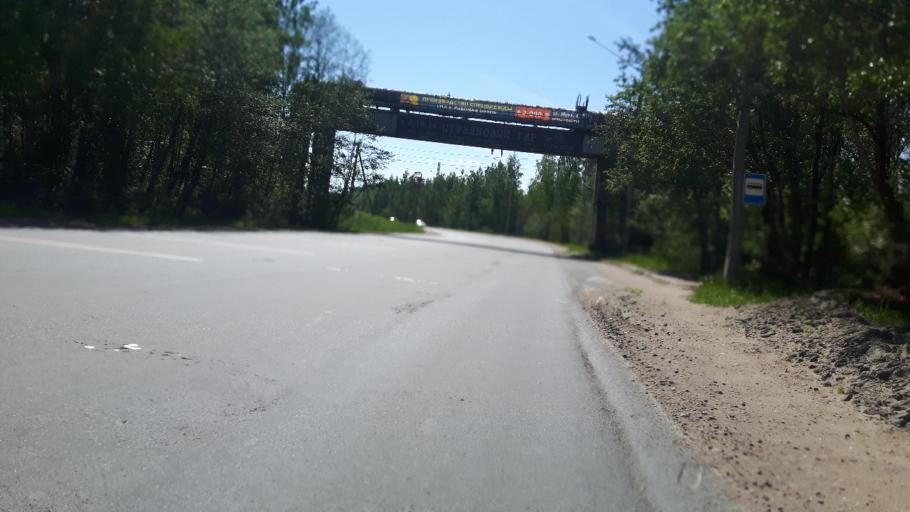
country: RU
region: Leningrad
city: Sosnovyy Bor
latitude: 59.8646
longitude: 29.0690
